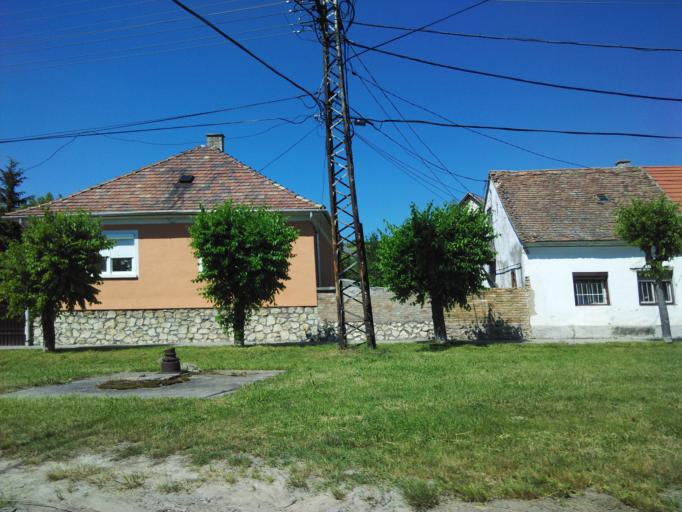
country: HU
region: Fejer
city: Mor
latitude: 47.3741
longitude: 18.2164
